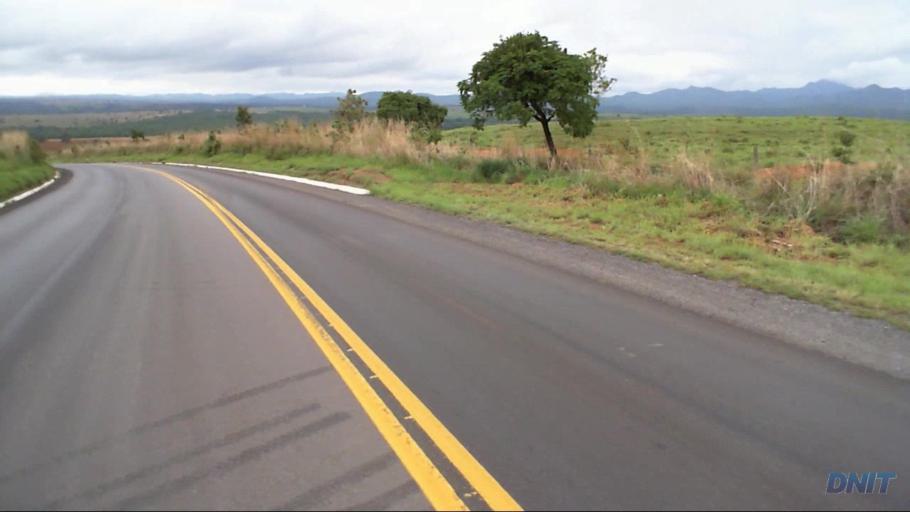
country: BR
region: Goias
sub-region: Padre Bernardo
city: Padre Bernardo
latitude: -15.2199
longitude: -48.5292
